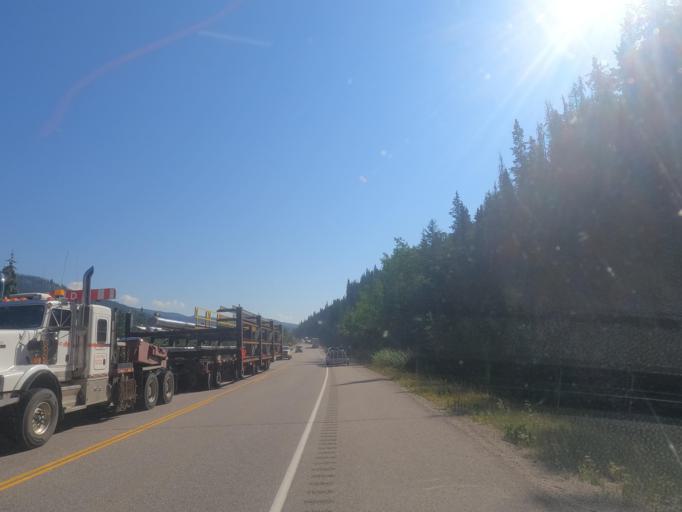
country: CA
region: Alberta
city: Jasper Park Lodge
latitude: 52.8727
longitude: -118.3002
